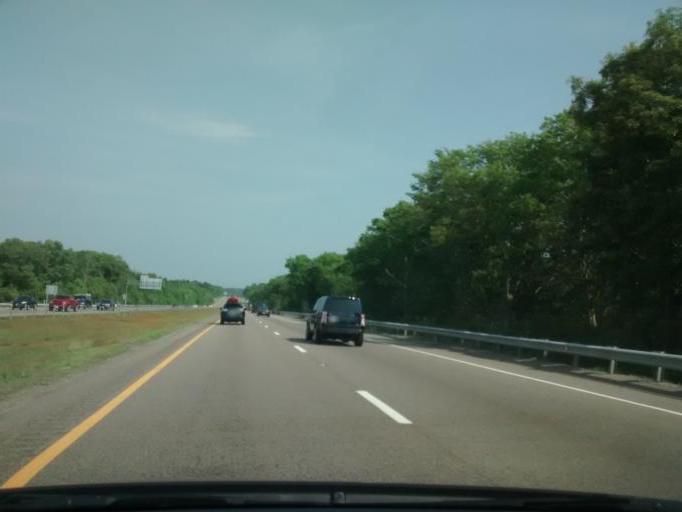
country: US
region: Massachusetts
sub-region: Plymouth County
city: Middleborough Center
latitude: 41.8816
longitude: -70.9192
